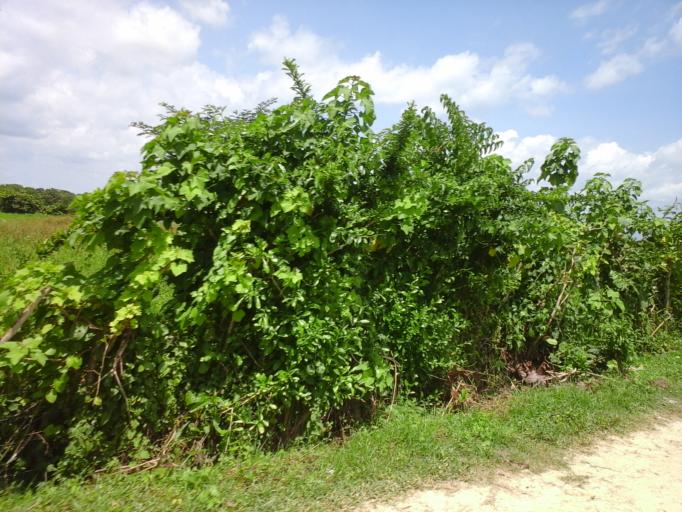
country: CO
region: Bolivar
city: San Pablo
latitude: 10.1499
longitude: -75.2768
